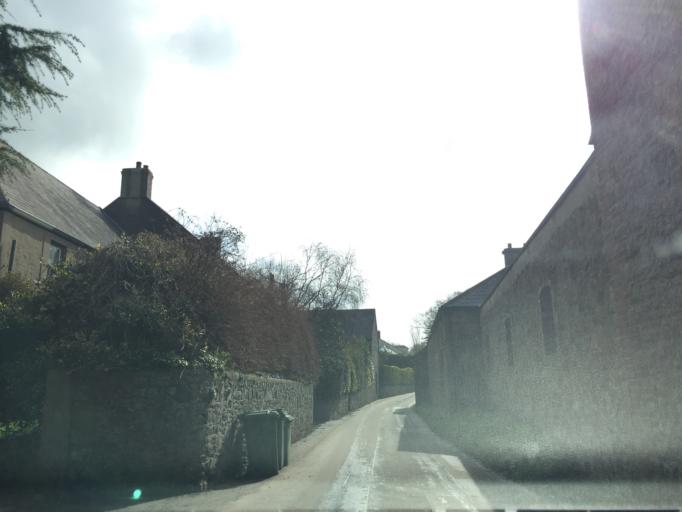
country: JE
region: St Helier
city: Saint Helier
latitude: 49.2027
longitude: -2.0684
